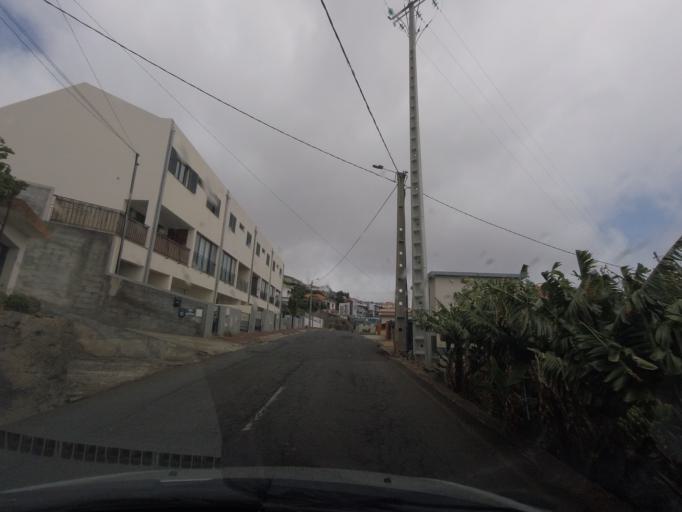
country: PT
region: Madeira
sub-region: Machico
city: Machico
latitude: 32.7025
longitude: -16.7768
